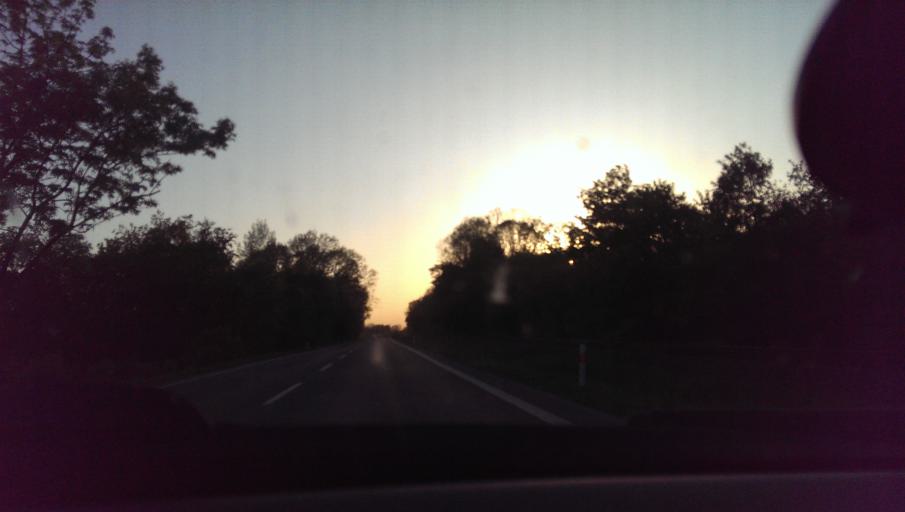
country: CZ
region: Zlin
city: Zubri
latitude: 49.4600
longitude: 18.1116
